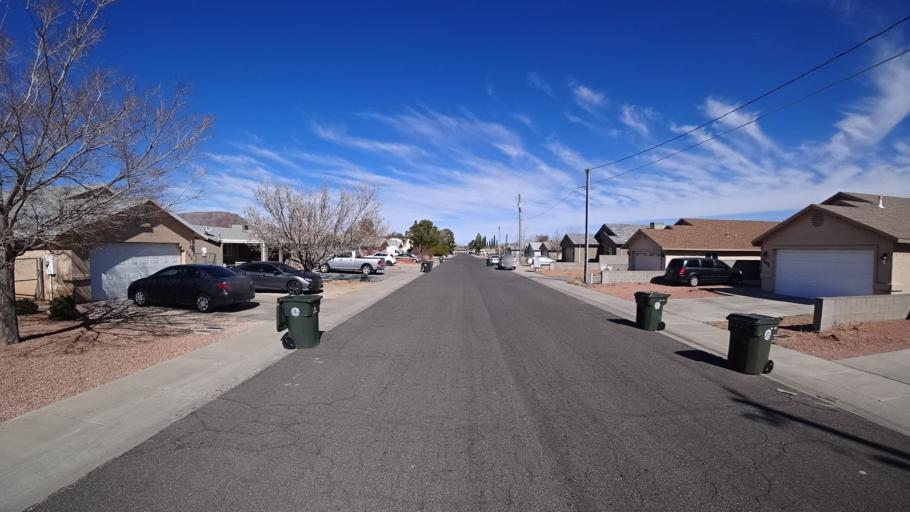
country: US
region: Arizona
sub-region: Mohave County
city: New Kingman-Butler
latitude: 35.2277
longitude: -114.0284
